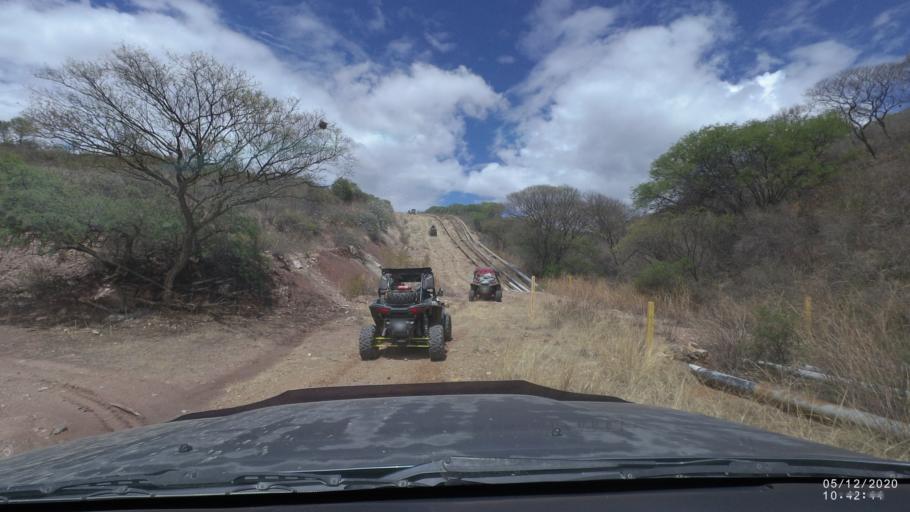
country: BO
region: Cochabamba
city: Sipe Sipe
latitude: -17.5476
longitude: -66.2955
